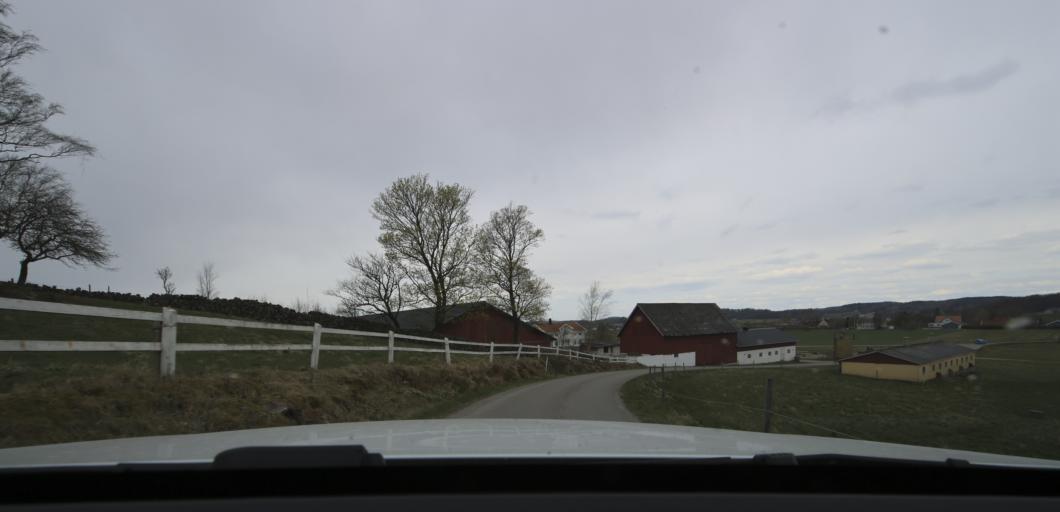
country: SE
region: Halland
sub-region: Varbergs Kommun
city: Tvaaker
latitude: 57.1299
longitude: 12.4562
